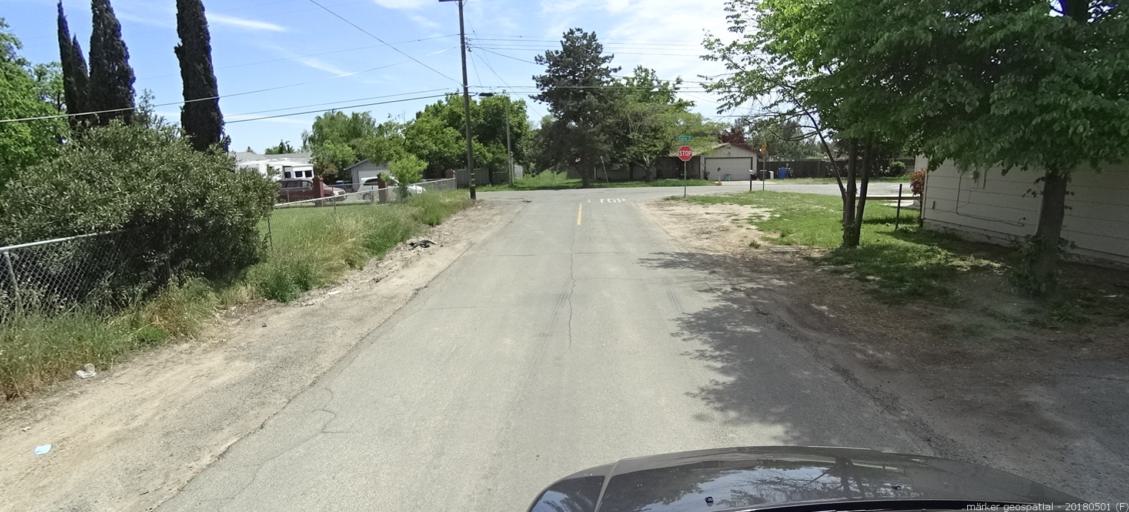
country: US
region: California
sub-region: Sacramento County
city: Rio Linda
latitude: 38.6624
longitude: -121.4431
